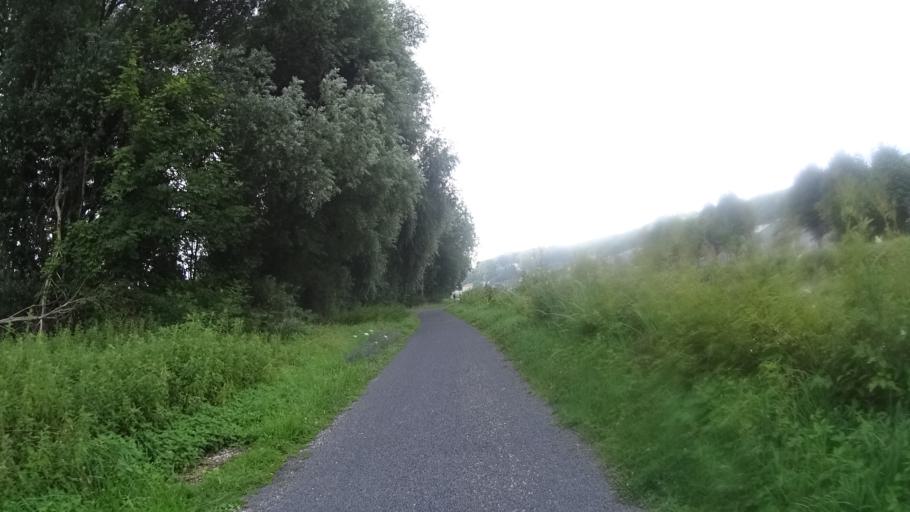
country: FR
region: Lorraine
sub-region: Departement de la Meuse
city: Fains-Veel
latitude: 48.7897
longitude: 5.1350
